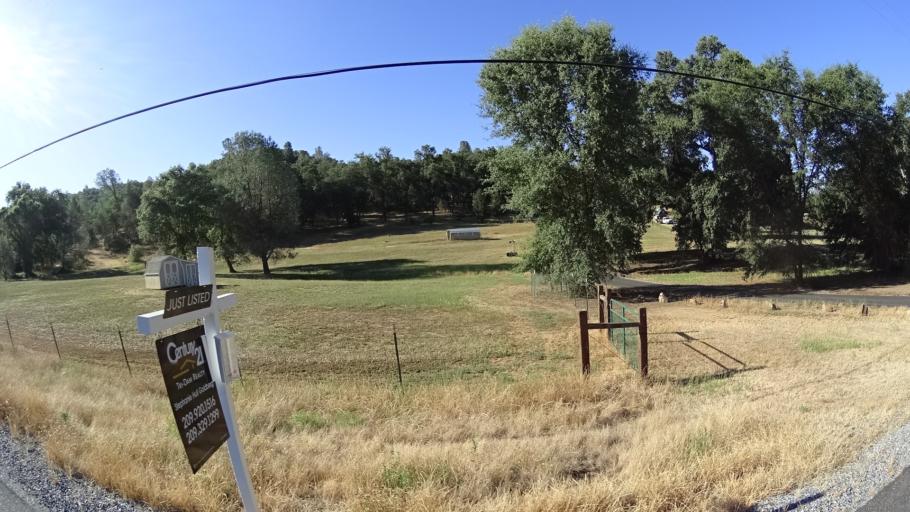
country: US
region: California
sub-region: Calaveras County
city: San Andreas
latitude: 38.2526
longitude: -120.7160
